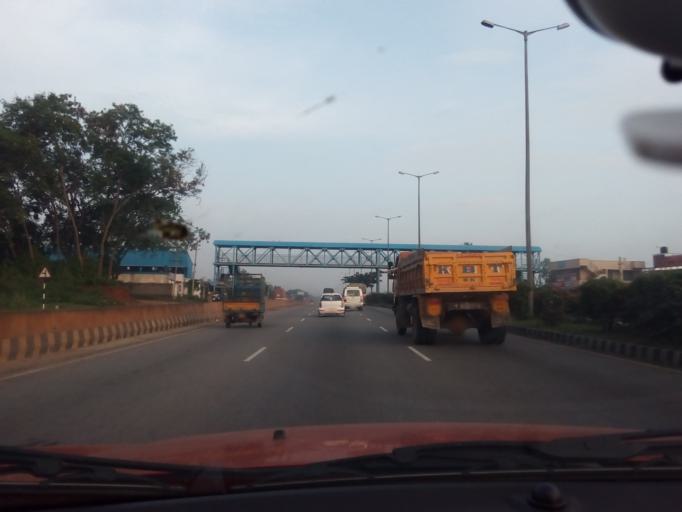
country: IN
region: Karnataka
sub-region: Bangalore Rural
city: Nelamangala
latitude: 13.0851
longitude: 77.4128
